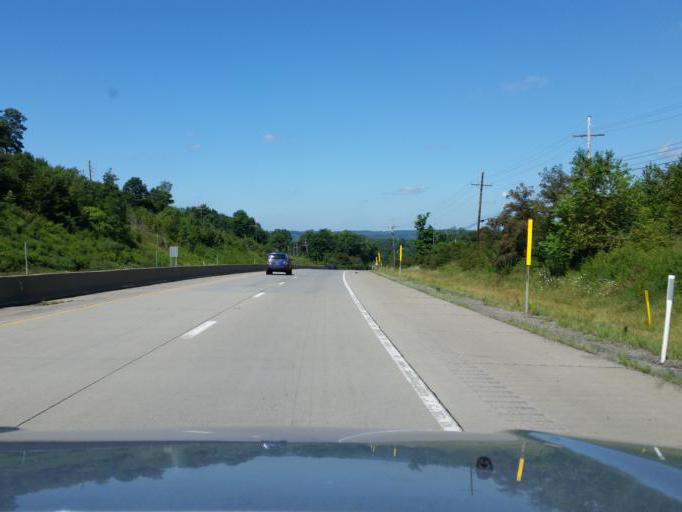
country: US
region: Pennsylvania
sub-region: Cambria County
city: Vinco
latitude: 40.4426
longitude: -78.9634
